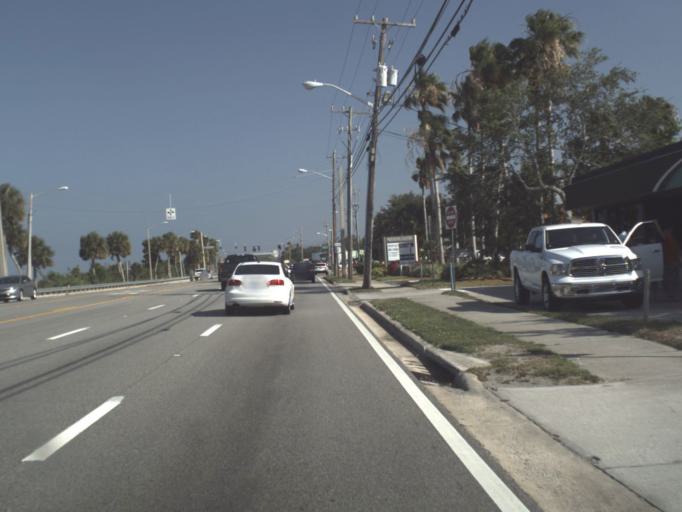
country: US
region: Florida
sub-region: Brevard County
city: Melbourne
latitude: 28.0959
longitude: -80.6112
